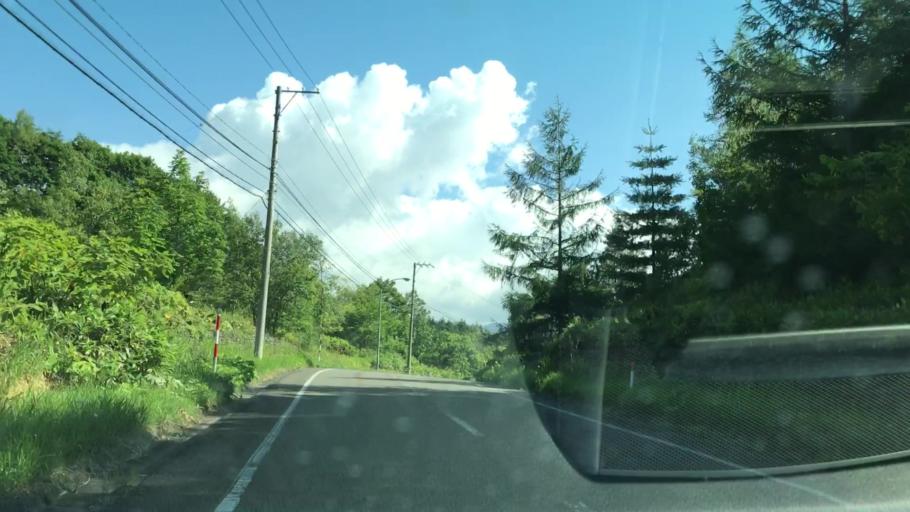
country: JP
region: Hokkaido
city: Shimo-furano
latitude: 42.8605
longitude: 142.4404
